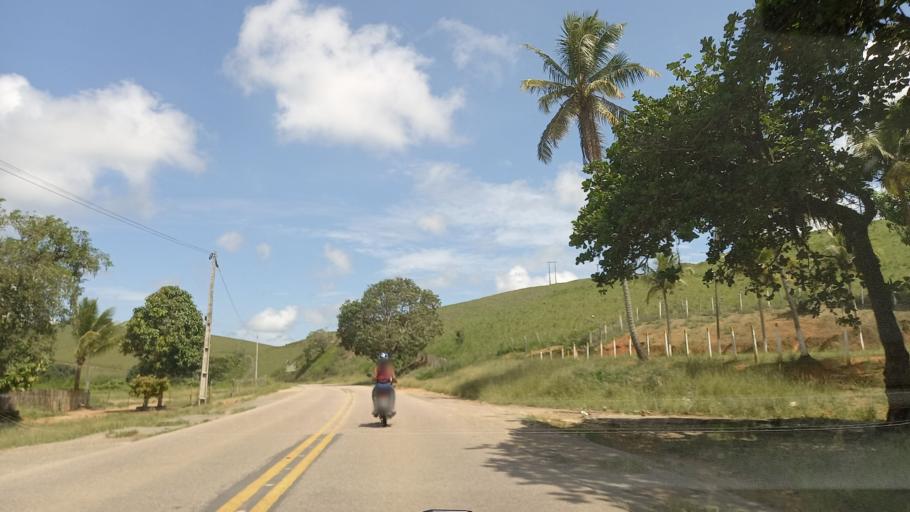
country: BR
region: Pernambuco
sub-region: Barreiros
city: Barreiros
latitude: -8.7512
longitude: -35.1719
